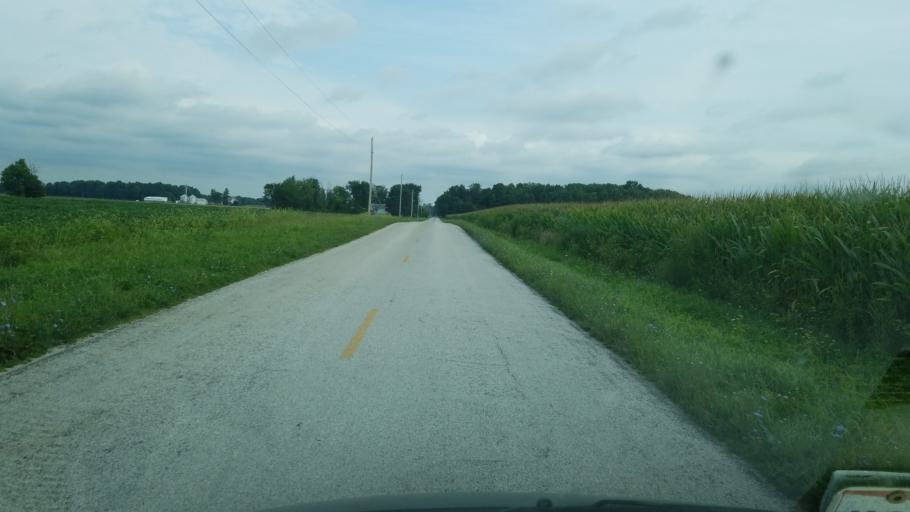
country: US
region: Ohio
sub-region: Seneca County
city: Tiffin
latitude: 41.1727
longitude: -83.1030
